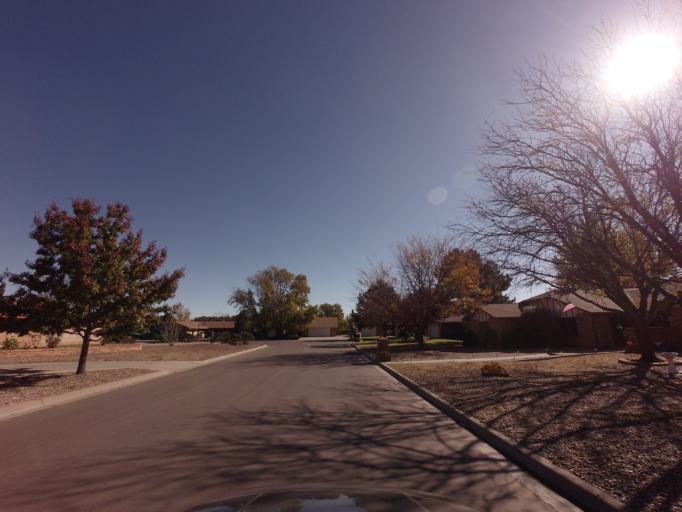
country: US
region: New Mexico
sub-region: Curry County
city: Clovis
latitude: 34.4234
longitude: -103.1899
